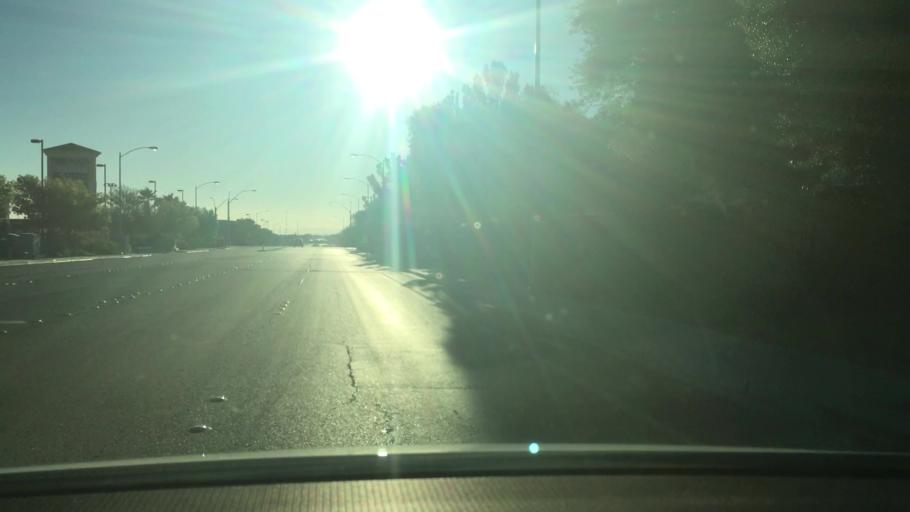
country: US
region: Nevada
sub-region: Clark County
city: Summerlin South
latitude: 36.0776
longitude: -115.2999
